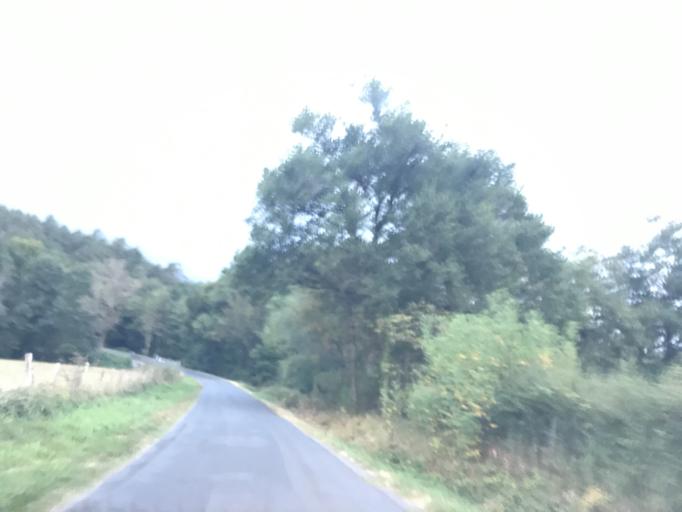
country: FR
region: Auvergne
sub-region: Departement du Puy-de-Dome
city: Escoutoux
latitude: 45.7933
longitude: 3.5737
